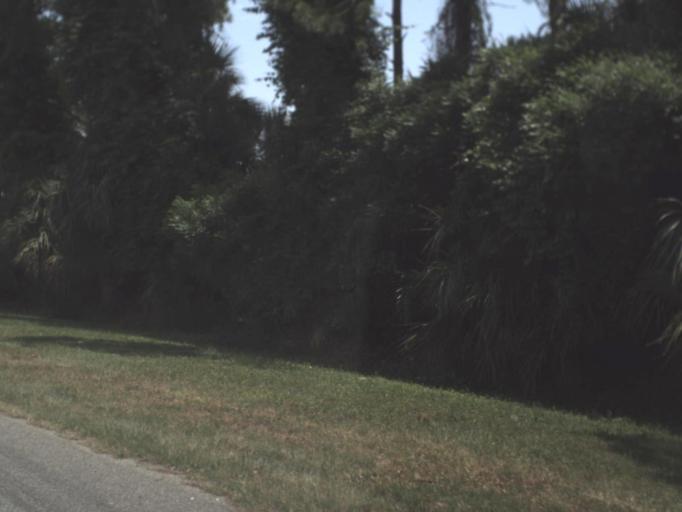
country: US
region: Florida
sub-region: Saint Johns County
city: Ponte Vedra Beach
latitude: 30.2442
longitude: -81.3875
